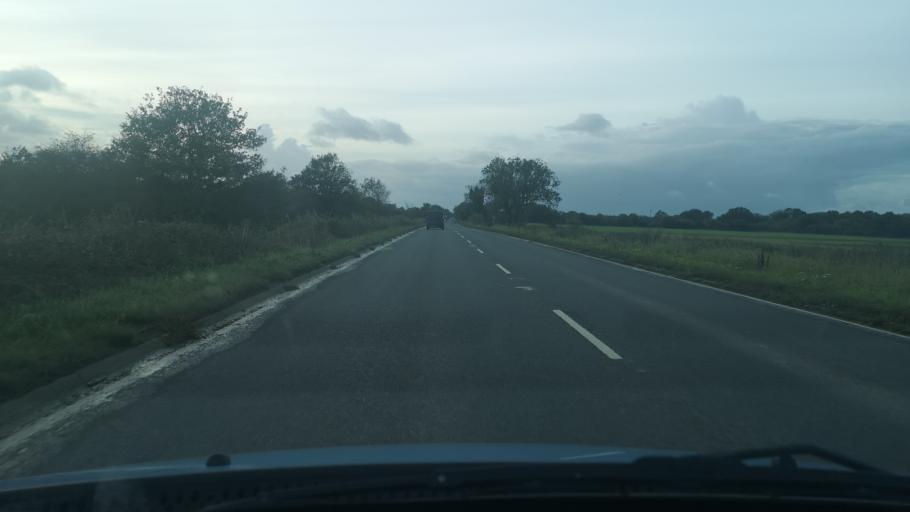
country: GB
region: England
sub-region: North Lincolnshire
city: Belton
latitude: 53.5818
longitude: -0.7990
